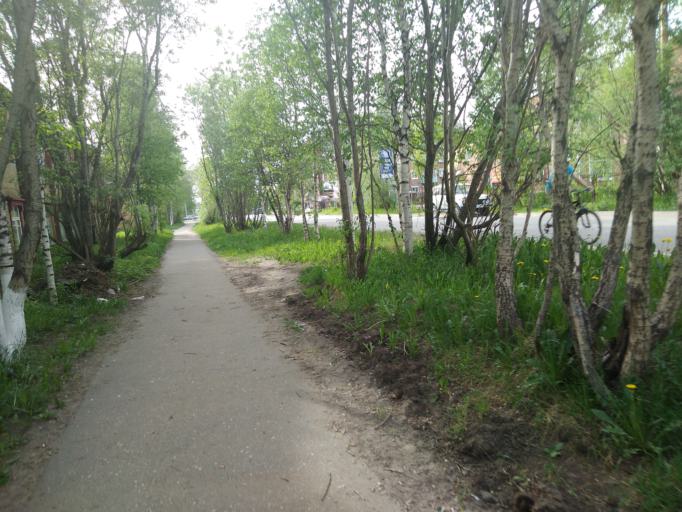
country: RU
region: Komi Republic
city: Pechora
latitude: 65.1459
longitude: 57.2233
